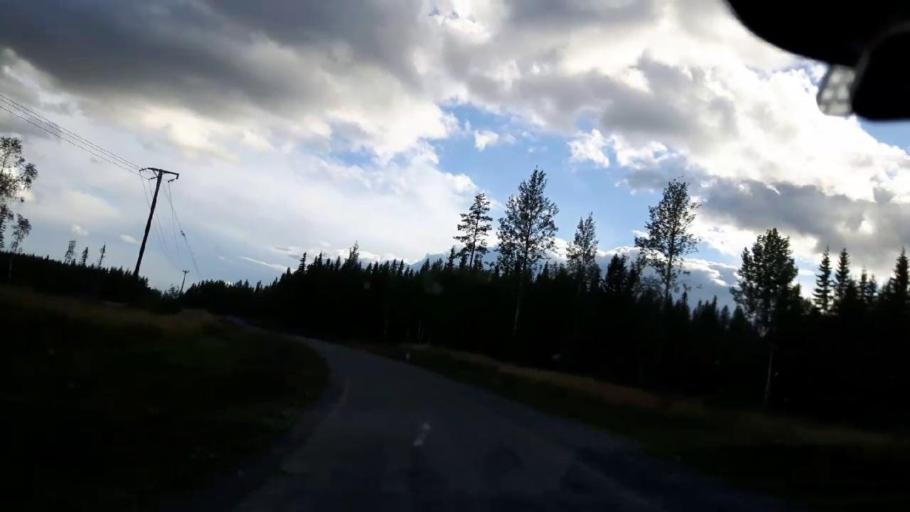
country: SE
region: Jaemtland
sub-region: Stroemsunds Kommun
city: Stroemsund
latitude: 63.3321
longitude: 15.5786
